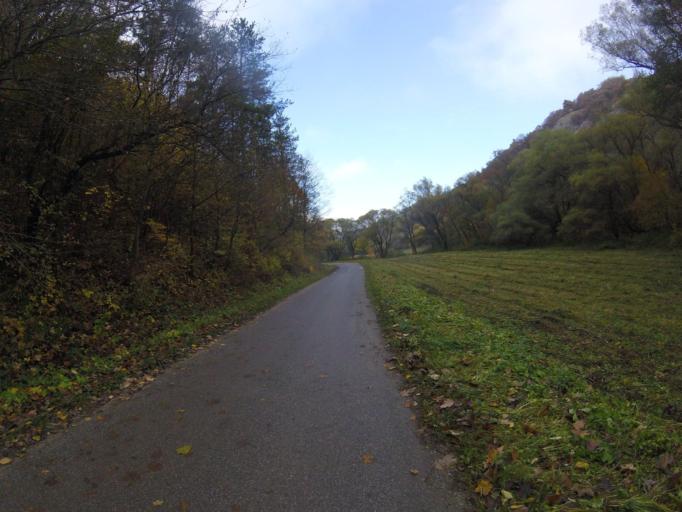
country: HU
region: Borsod-Abauj-Zemplen
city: Putnok
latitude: 48.2138
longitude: 20.4443
